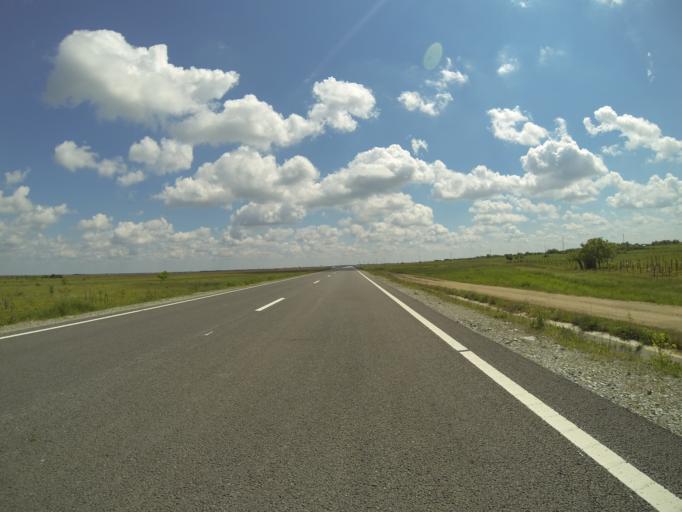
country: RO
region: Dolj
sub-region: Comuna Carcea
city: Carcea
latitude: 44.2775
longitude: 23.9089
